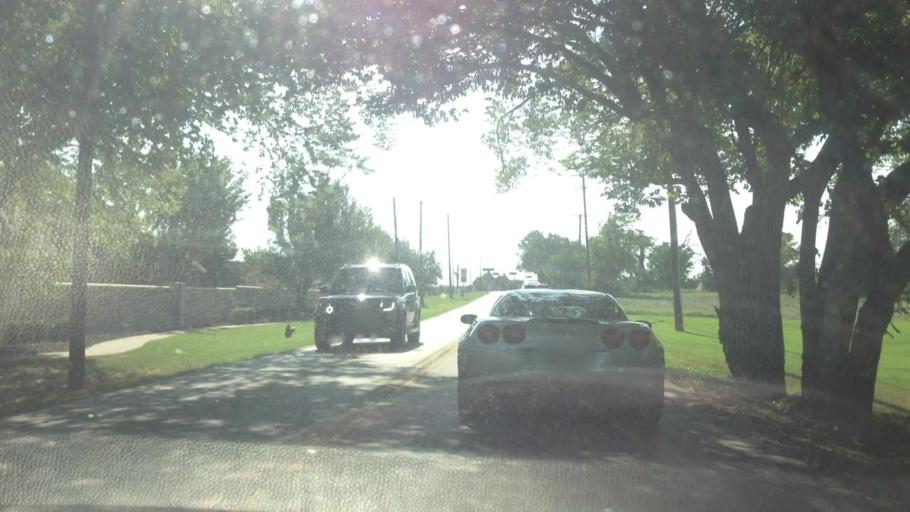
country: US
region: Texas
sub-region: Tarrant County
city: Colleyville
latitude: 32.8926
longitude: -97.1835
